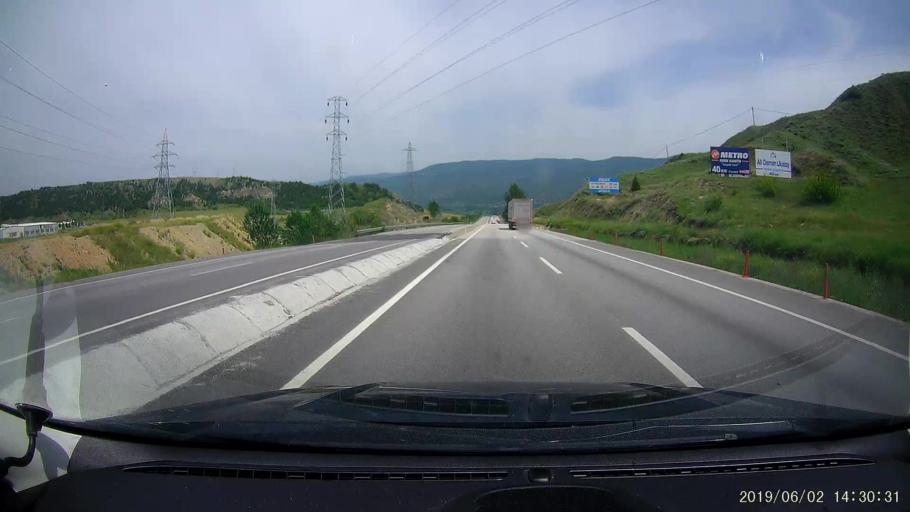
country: TR
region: Kastamonu
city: Tosya
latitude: 41.0172
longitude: 34.1169
